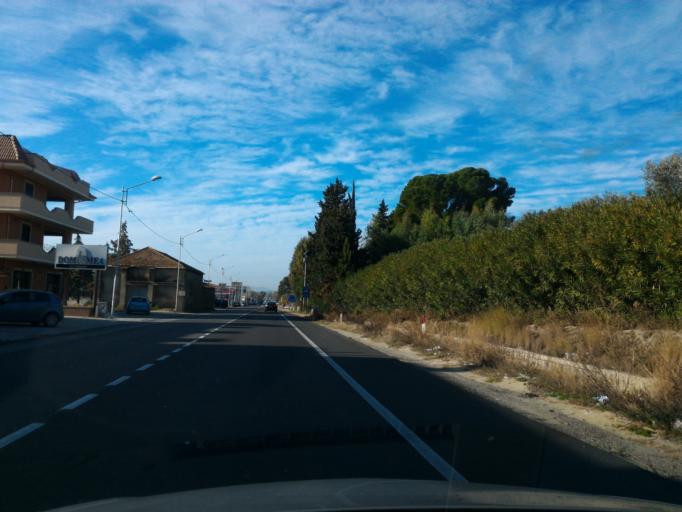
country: IT
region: Calabria
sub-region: Provincia di Catanzaro
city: Botricello
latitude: 38.9321
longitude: 16.8449
